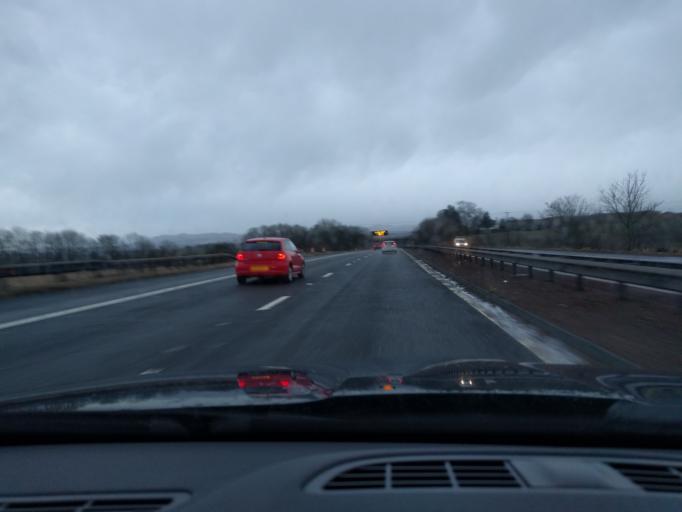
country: GB
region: Scotland
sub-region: West Lothian
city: Broxburn
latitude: 55.9647
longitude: -3.4459
